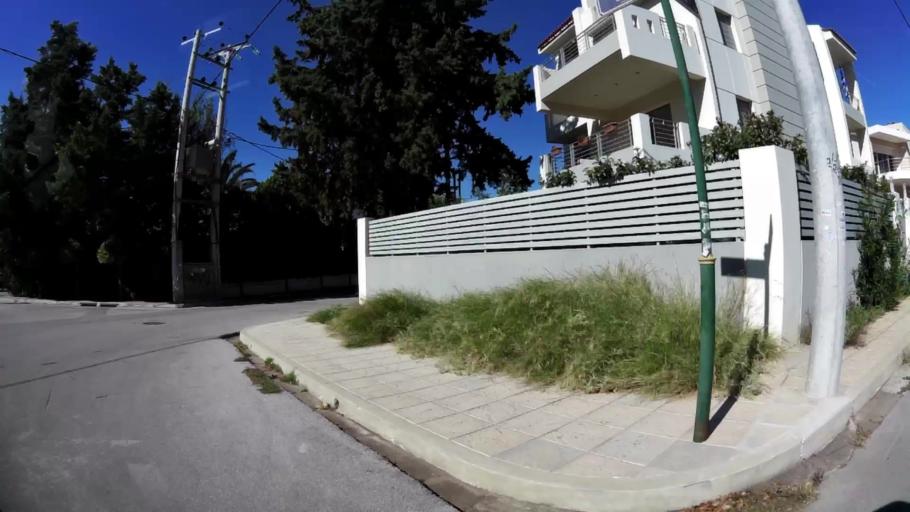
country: GR
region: Attica
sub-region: Nomarchia Athinas
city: Kifisia
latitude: 38.0826
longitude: 23.8020
